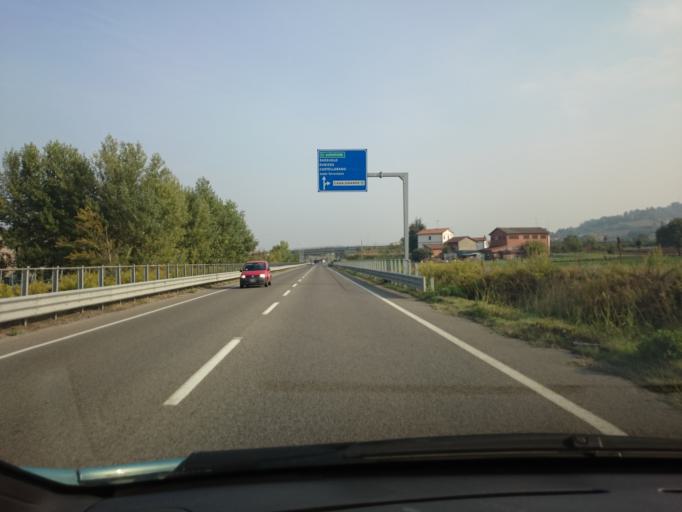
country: IT
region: Emilia-Romagna
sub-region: Provincia di Reggio Emilia
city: Casalgrande
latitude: 44.5874
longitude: 10.7224
